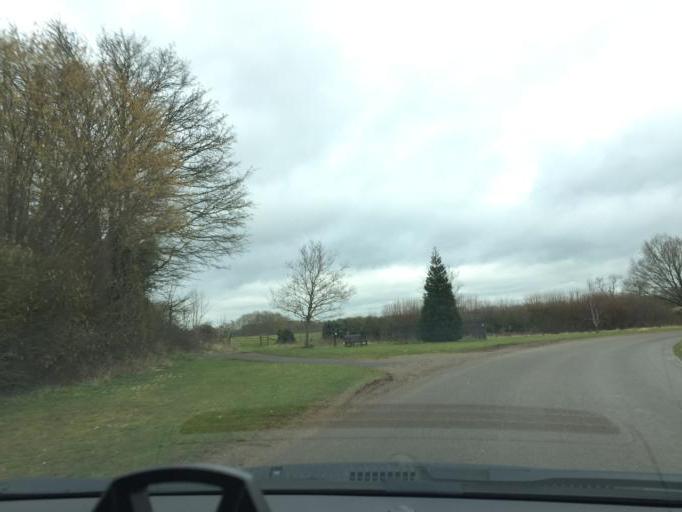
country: GB
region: England
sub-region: Northamptonshire
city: Silverstone
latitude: 52.0749
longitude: -1.0795
